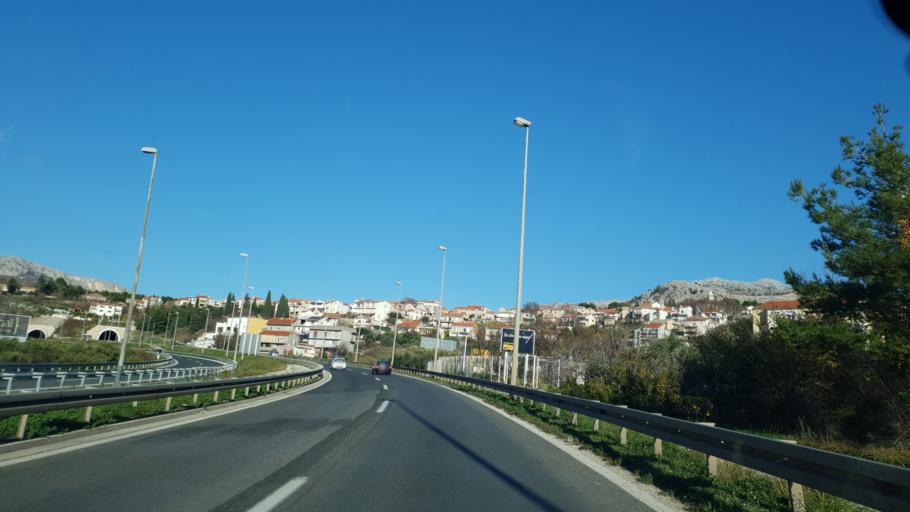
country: HR
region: Splitsko-Dalmatinska
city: Mravince
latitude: 43.5295
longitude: 16.5102
